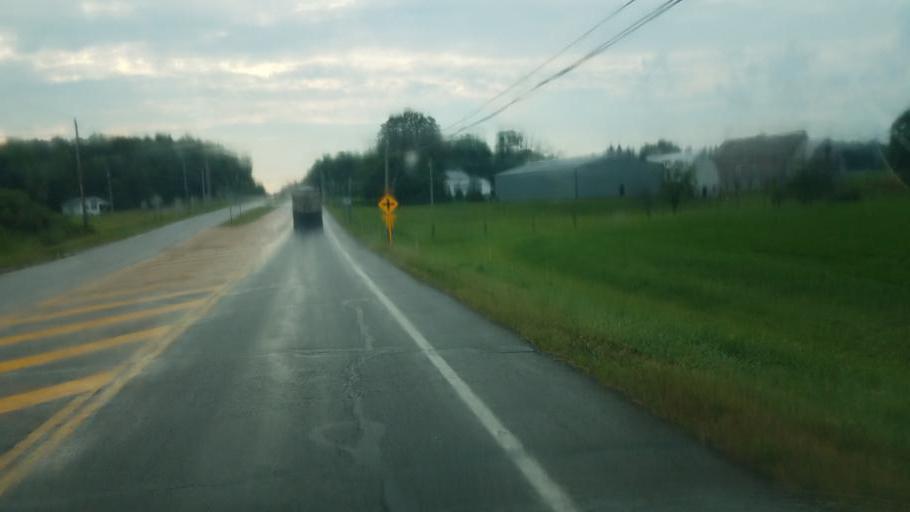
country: US
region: Ohio
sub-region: Portage County
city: Hiram
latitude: 41.3775
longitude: -81.1107
